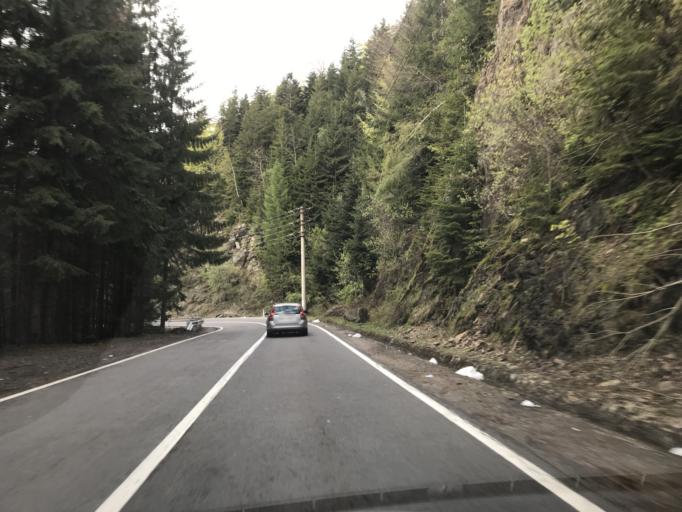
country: RO
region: Sibiu
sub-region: Comuna Cartisoara
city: Cartisoara
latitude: 45.6536
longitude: 24.6036
